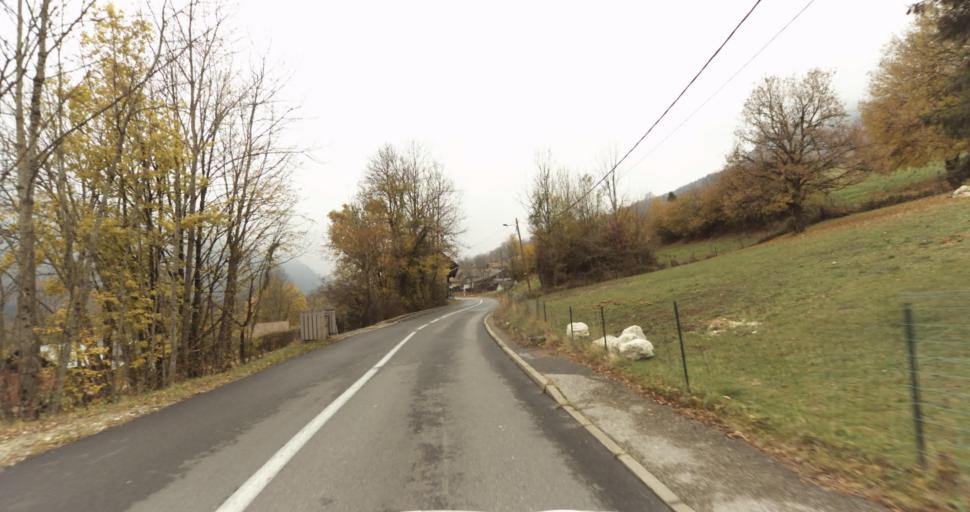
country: FR
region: Rhone-Alpes
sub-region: Departement de la Haute-Savoie
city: Gruffy
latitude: 45.7497
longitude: 6.0850
